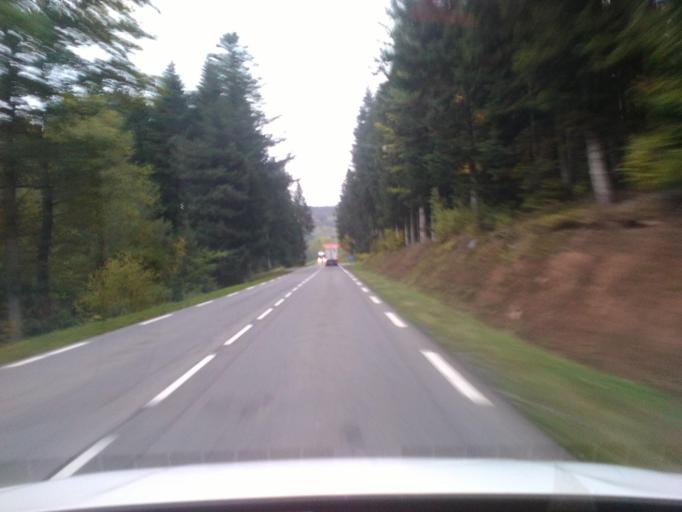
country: FR
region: Lorraine
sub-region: Departement des Vosges
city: Ban-de-Laveline
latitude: 48.3231
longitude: 7.0926
